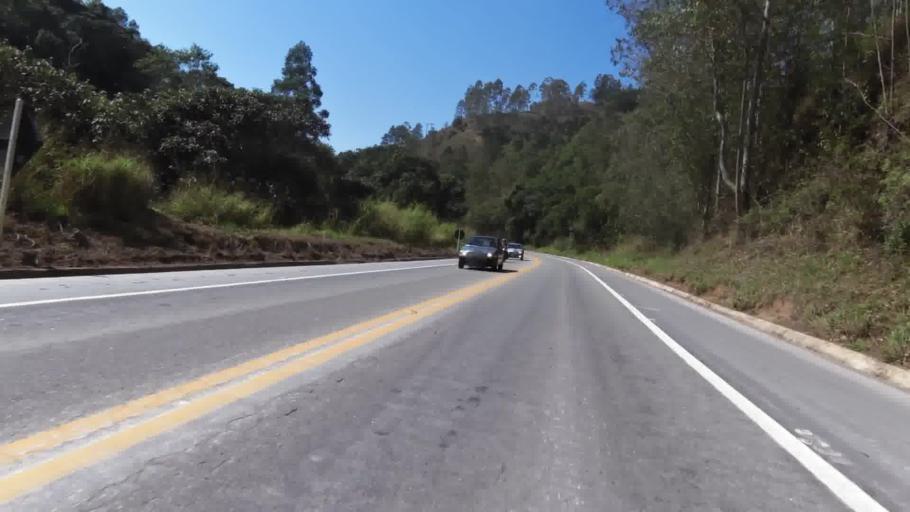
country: BR
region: Espirito Santo
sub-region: Marechal Floriano
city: Marechal Floriano
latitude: -20.4131
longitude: -40.8568
